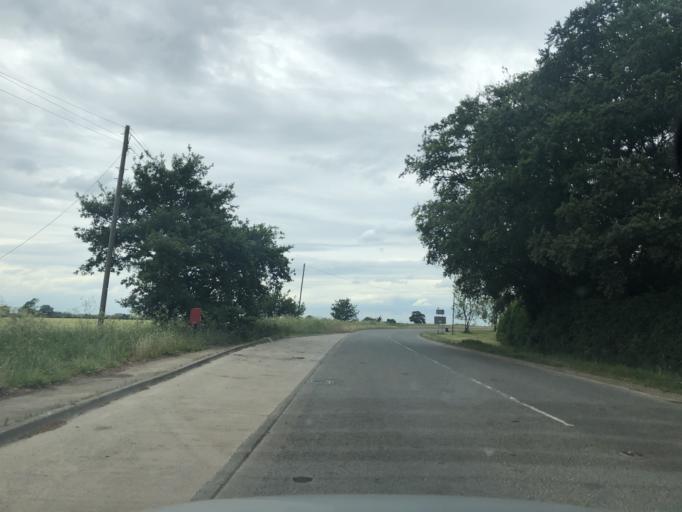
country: GB
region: England
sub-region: North Yorkshire
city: Thirsk
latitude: 54.2084
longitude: -1.3589
